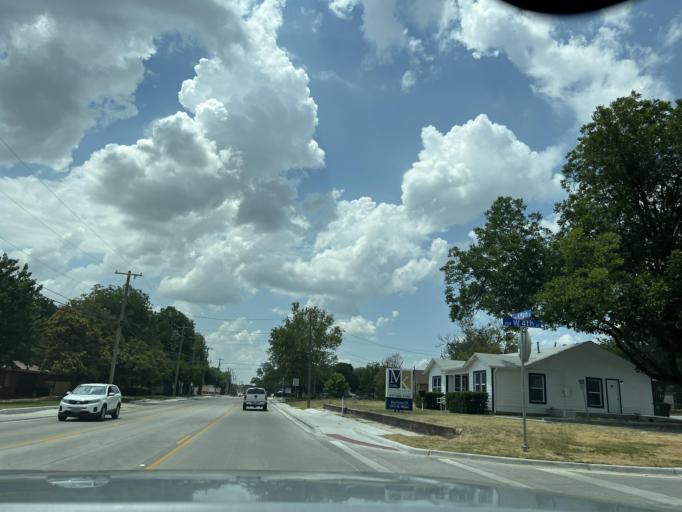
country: US
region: Texas
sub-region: Parker County
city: Springtown
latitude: 32.9691
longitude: -97.6845
